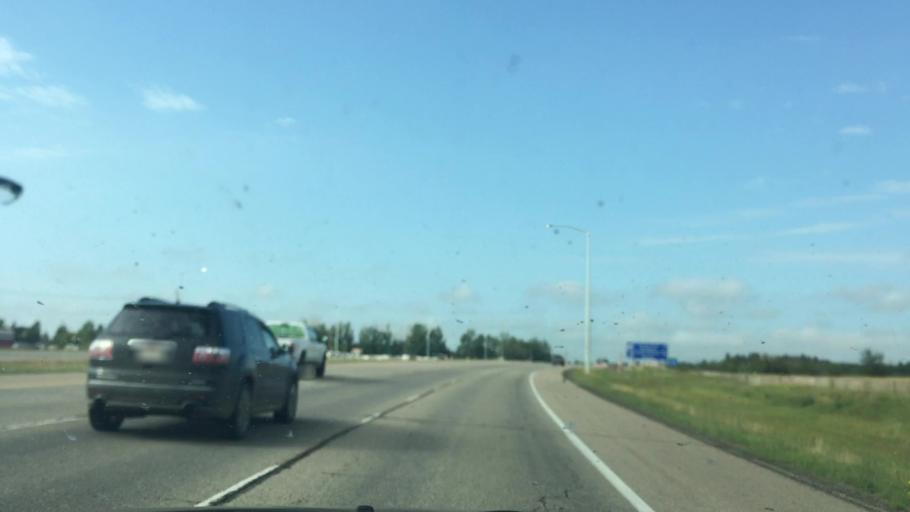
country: CA
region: Alberta
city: Leduc
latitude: 53.2779
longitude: -113.5526
